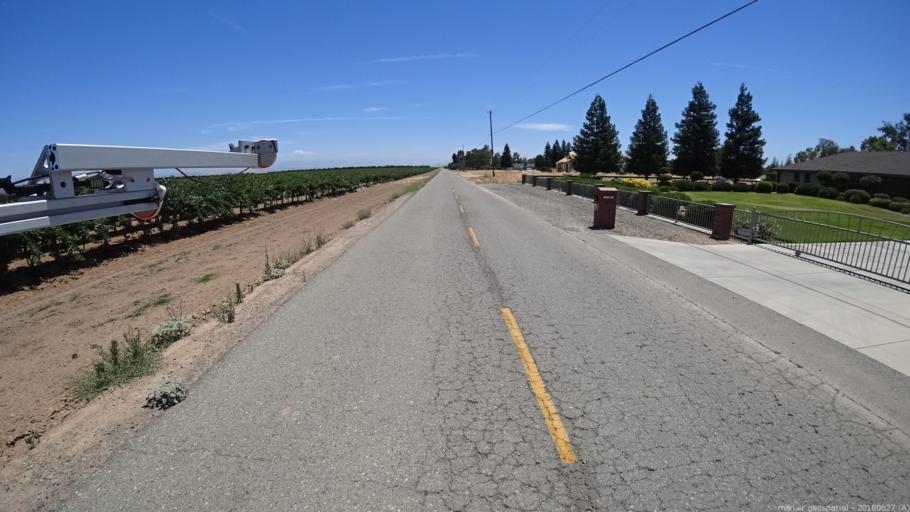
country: US
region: California
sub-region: Madera County
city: Bonadelle Ranchos-Madera Ranchos
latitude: 36.9375
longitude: -119.8655
